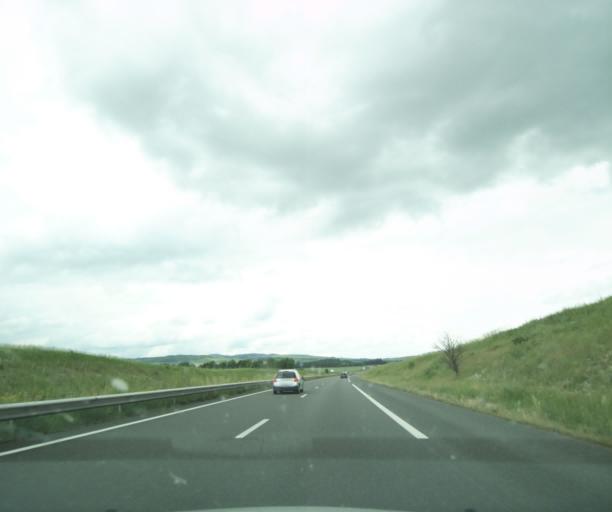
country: FR
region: Auvergne
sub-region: Departement du Puy-de-Dome
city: Saint-Bonnet-pres-Riom
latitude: 45.9360
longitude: 3.1282
